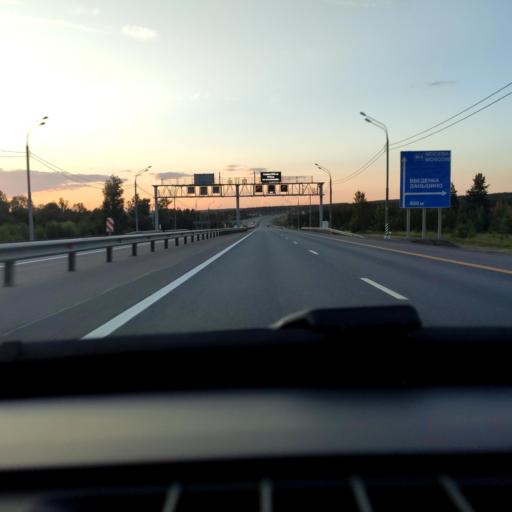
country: RU
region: Lipetsk
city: Khlevnoye
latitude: 52.2808
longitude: 39.0536
